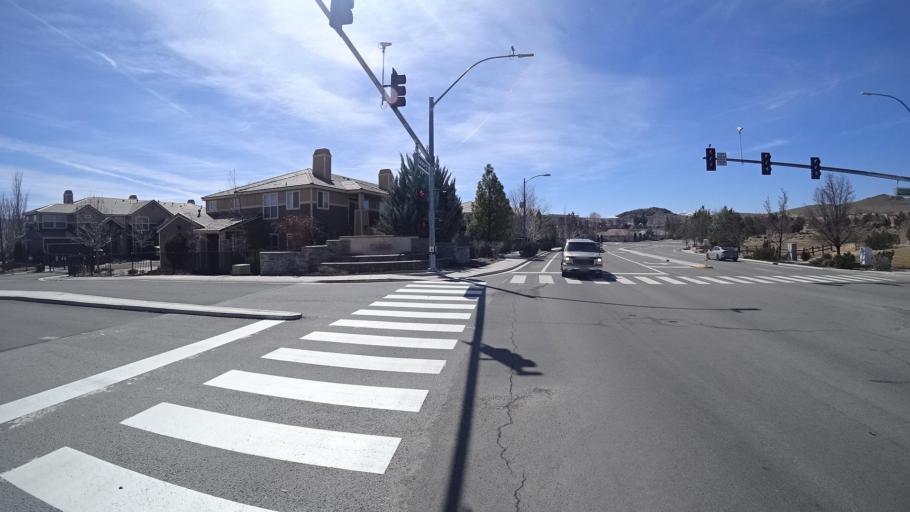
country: US
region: Nevada
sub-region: Washoe County
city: Sun Valley
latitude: 39.5821
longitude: -119.7370
